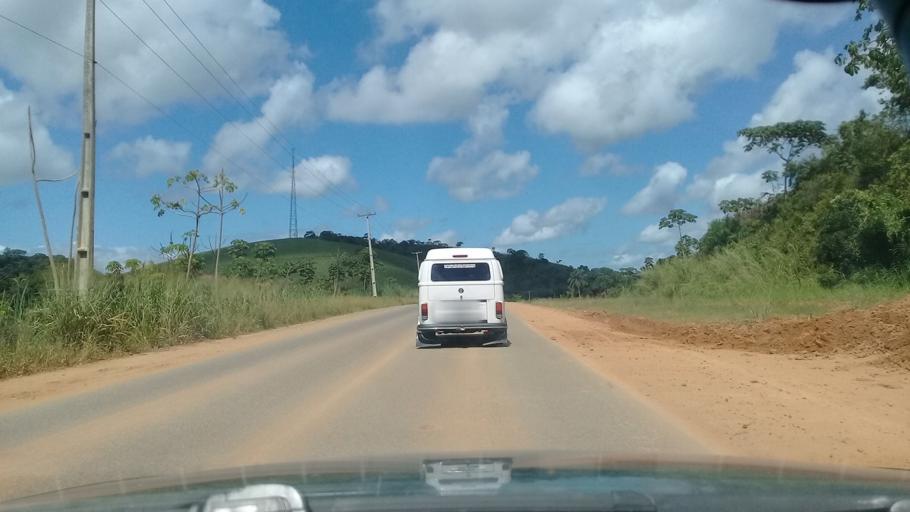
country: BR
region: Pernambuco
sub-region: Ipojuca
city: Ipojuca
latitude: -8.4914
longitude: -35.0919
